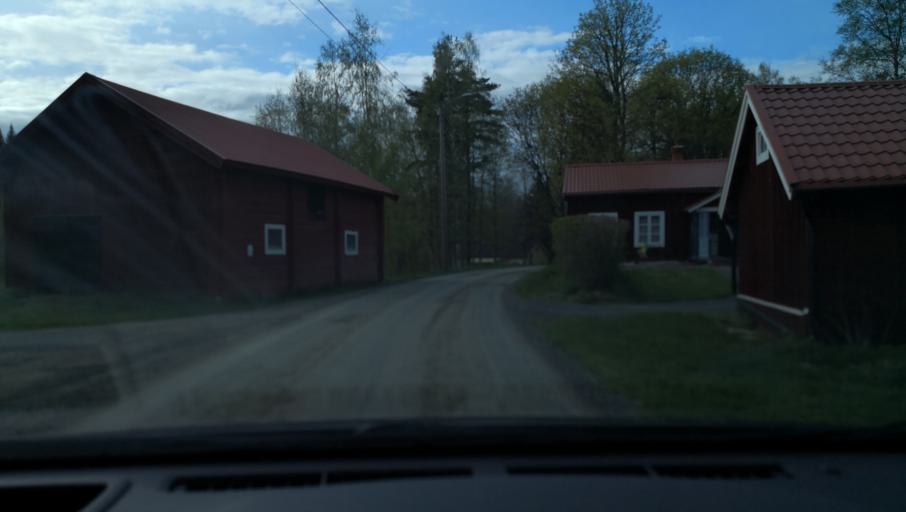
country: SE
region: Dalarna
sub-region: Saters Kommun
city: Saeter
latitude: 60.2654
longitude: 15.8284
